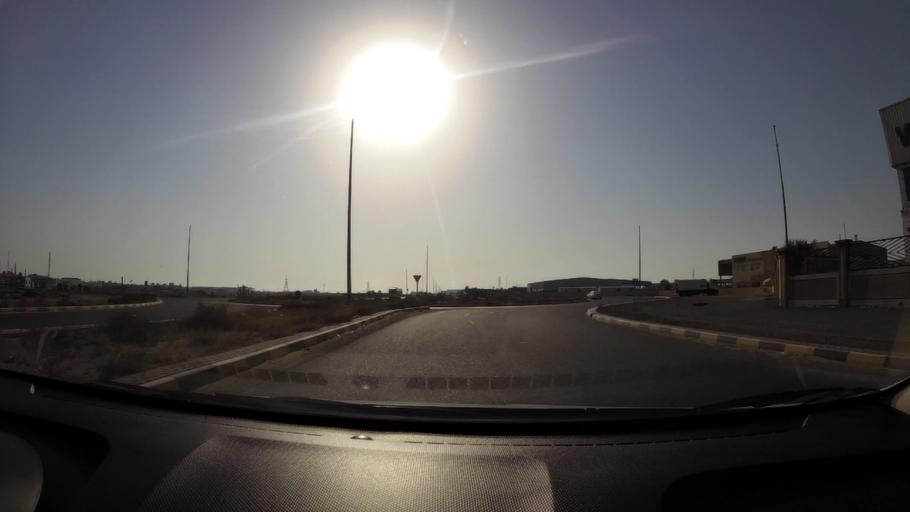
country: AE
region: Umm al Qaywayn
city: Umm al Qaywayn
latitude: 25.4445
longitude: 55.5508
